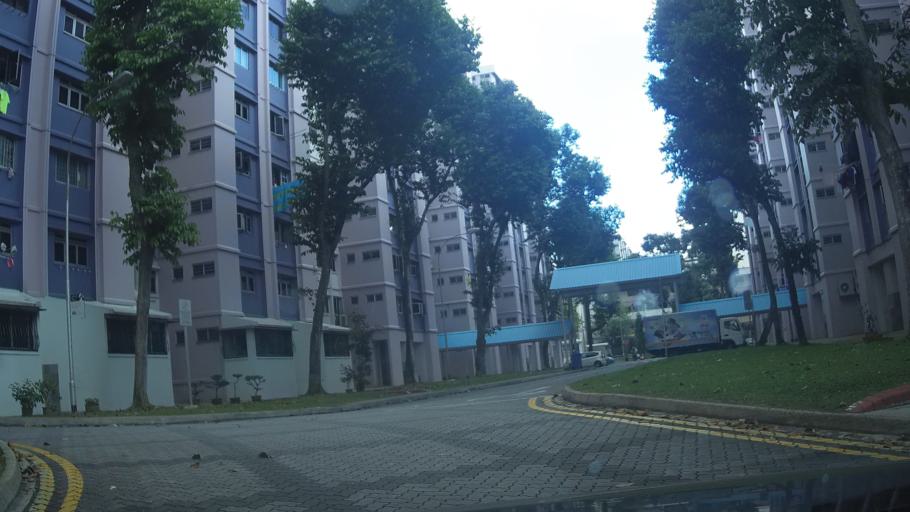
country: MY
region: Johor
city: Johor Bahru
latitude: 1.4416
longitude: 103.7896
